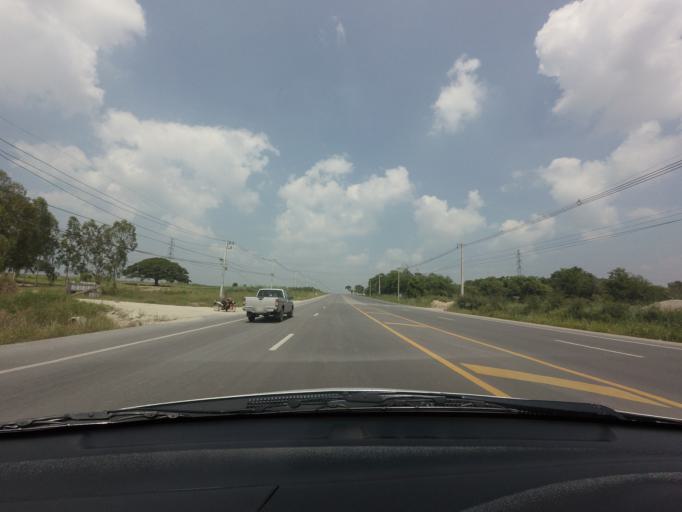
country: TH
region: Nakhon Ratchasima
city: Pak Chong
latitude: 14.6624
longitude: 101.4599
